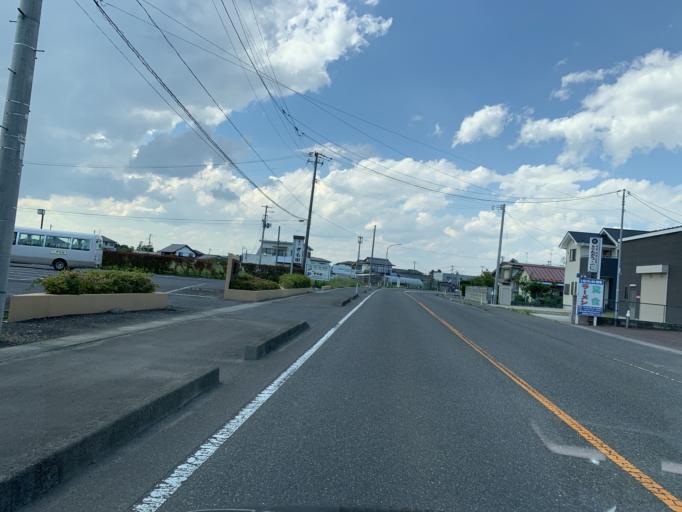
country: JP
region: Miyagi
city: Wakuya
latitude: 38.5025
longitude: 141.1194
